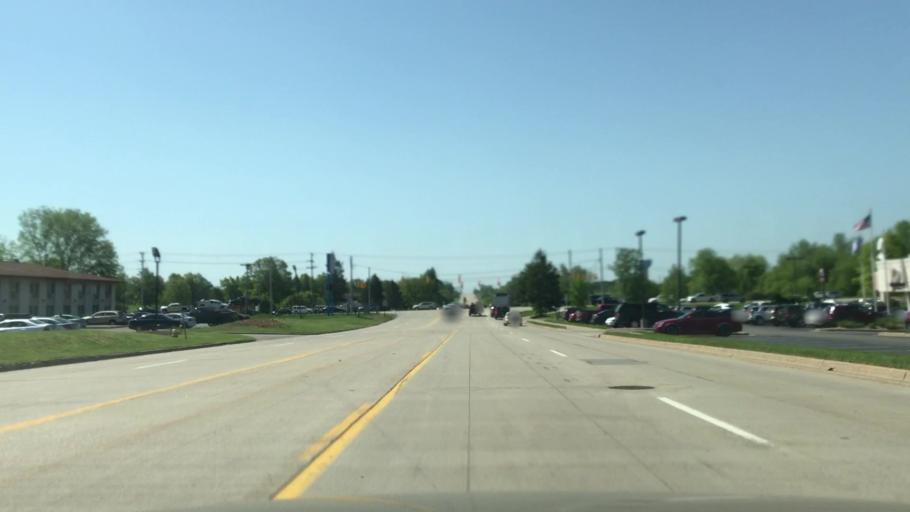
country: US
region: Michigan
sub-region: Kent County
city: East Grand Rapids
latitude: 42.9141
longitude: -85.5491
